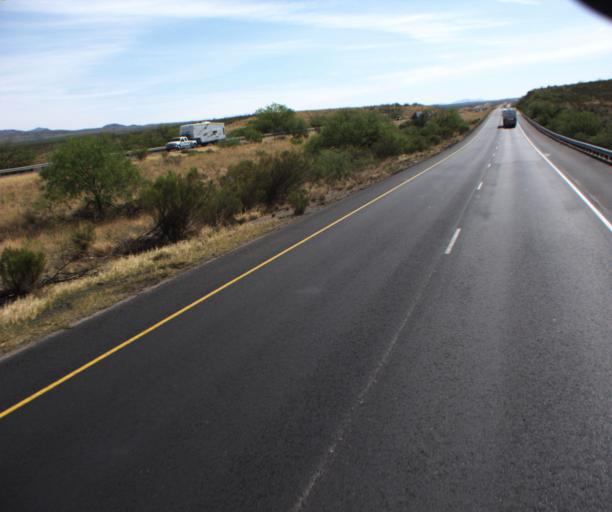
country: US
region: Arizona
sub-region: Pima County
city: Vail
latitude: 31.9878
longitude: -110.5875
